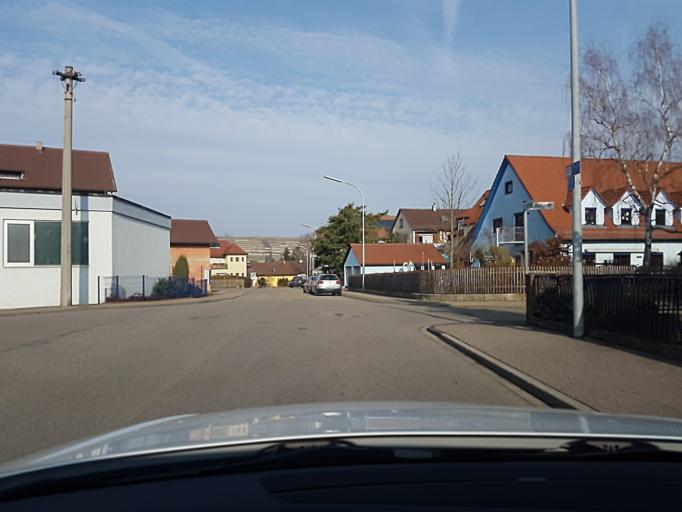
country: DE
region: Baden-Wuerttemberg
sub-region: Regierungsbezirk Stuttgart
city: Lauffen am Neckar
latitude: 49.0723
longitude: 9.1401
